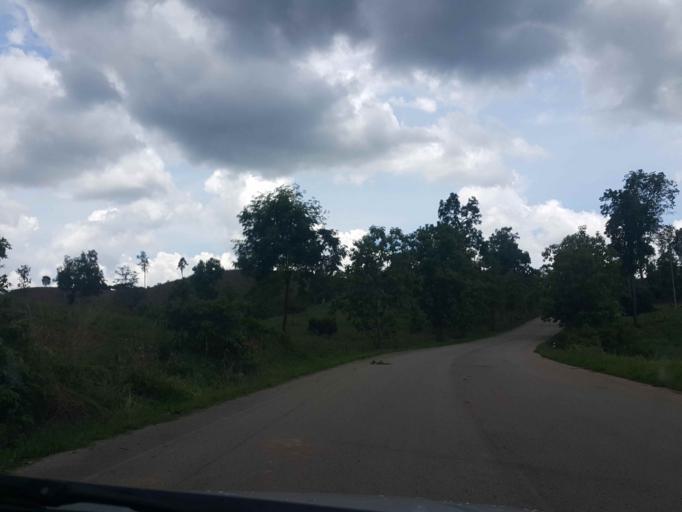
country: TH
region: Phayao
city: Dok Kham Tai
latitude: 18.9617
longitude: 100.0743
